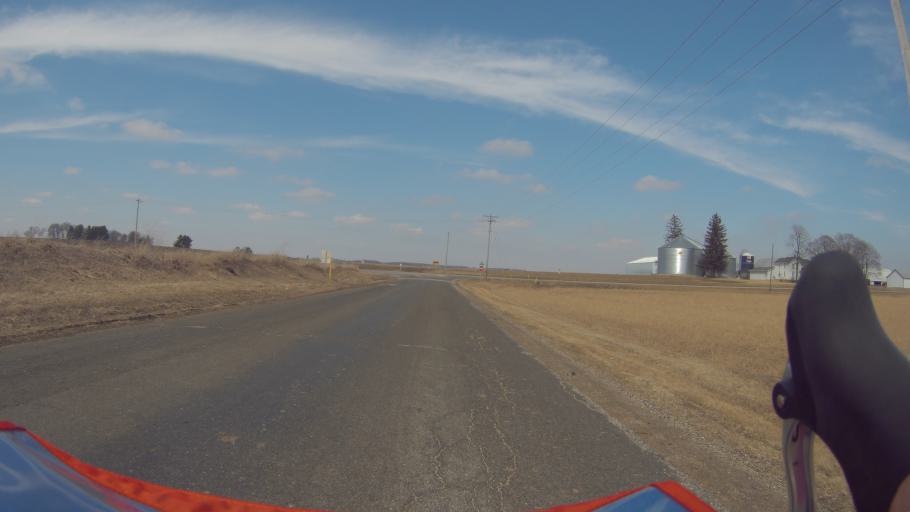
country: US
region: Wisconsin
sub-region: Dane County
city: Waunakee
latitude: 43.1619
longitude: -89.4925
